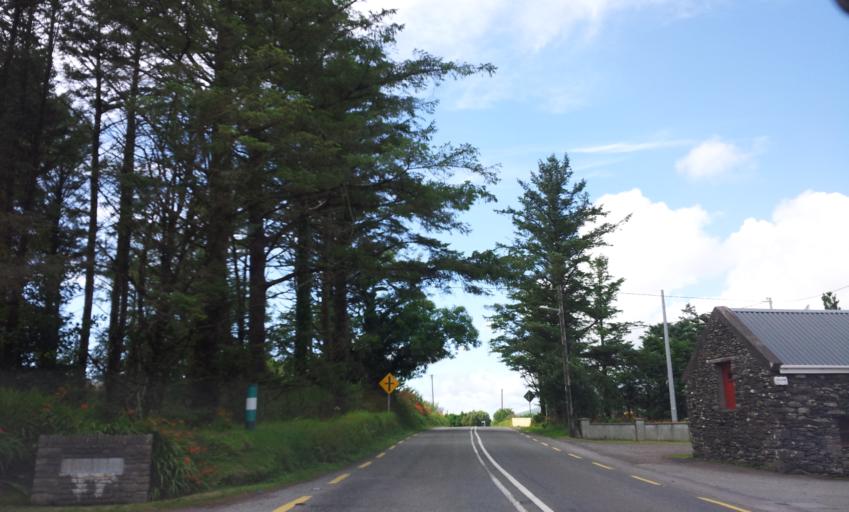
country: IE
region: Munster
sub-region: Ciarrai
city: Dingle
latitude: 52.1447
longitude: -10.1335
